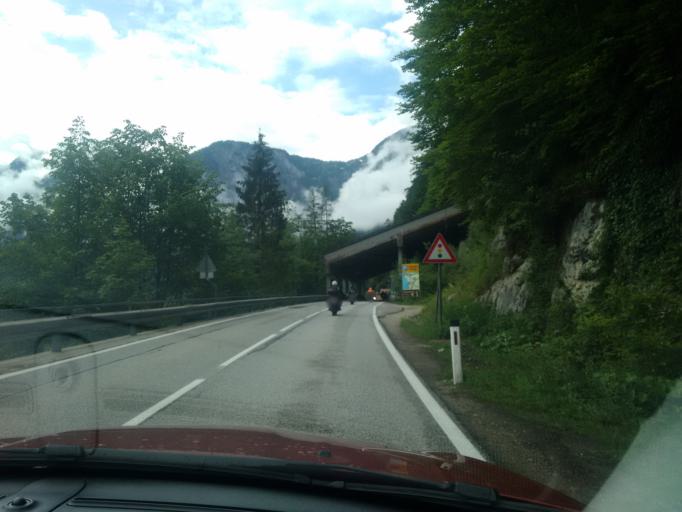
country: AT
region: Upper Austria
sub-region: Politischer Bezirk Gmunden
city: Bad Goisern
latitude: 47.5704
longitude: 13.6497
